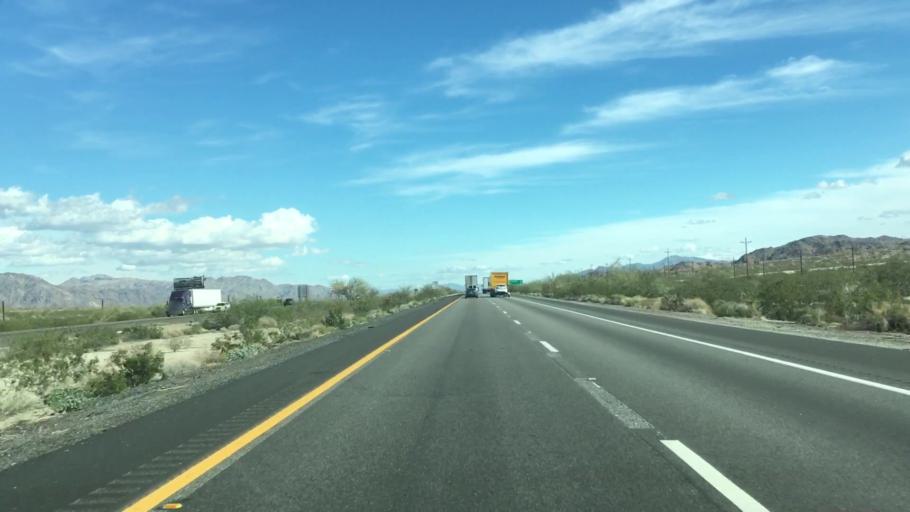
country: US
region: California
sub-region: Riverside County
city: Mecca
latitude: 33.6610
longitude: -115.7143
